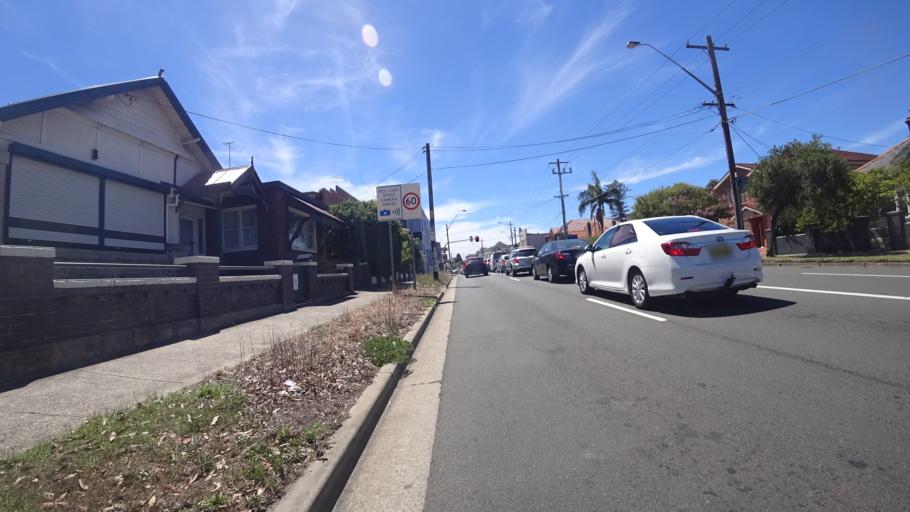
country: AU
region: New South Wales
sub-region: Rockdale
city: Bexley
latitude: -33.9490
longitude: 151.1285
